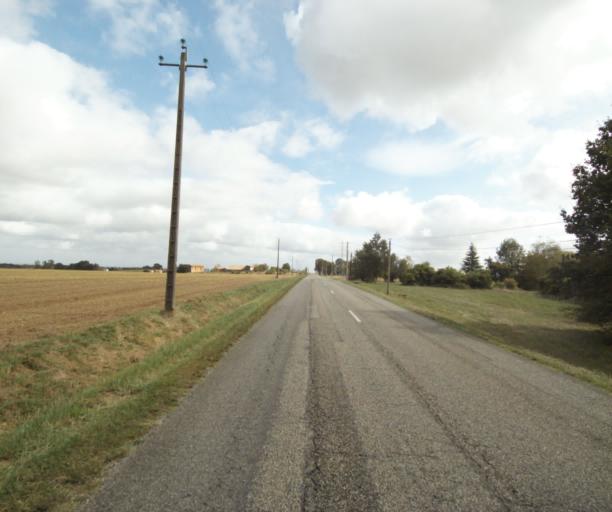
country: FR
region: Midi-Pyrenees
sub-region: Departement du Tarn-et-Garonne
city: Beaumont-de-Lomagne
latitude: 43.8652
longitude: 1.0753
